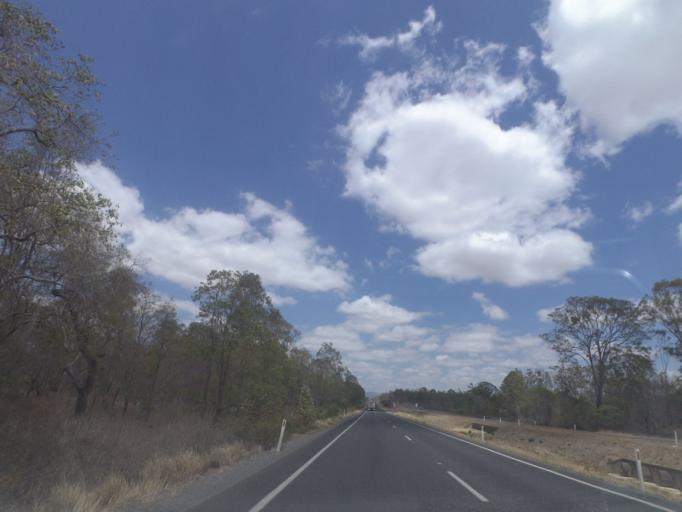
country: AU
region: Queensland
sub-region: Lockyer Valley
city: Gatton
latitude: -27.5517
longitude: 152.1469
